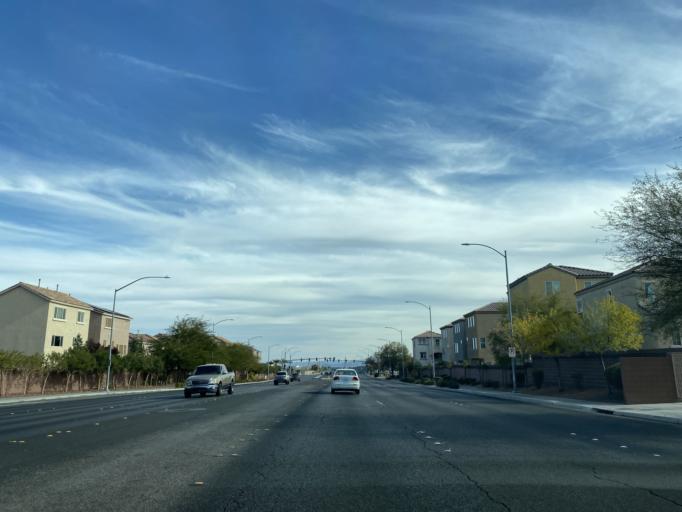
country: US
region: Nevada
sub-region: Clark County
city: Enterprise
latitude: 36.0563
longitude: -115.2278
